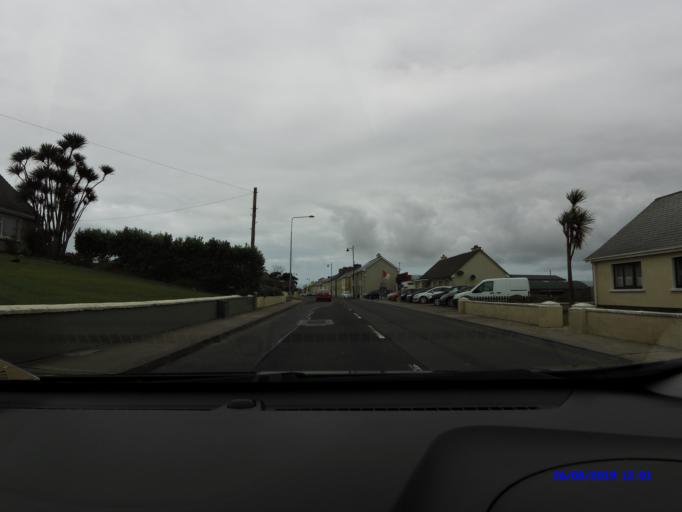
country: IE
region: Connaught
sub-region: Maigh Eo
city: Belmullet
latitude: 54.2221
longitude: -9.9819
